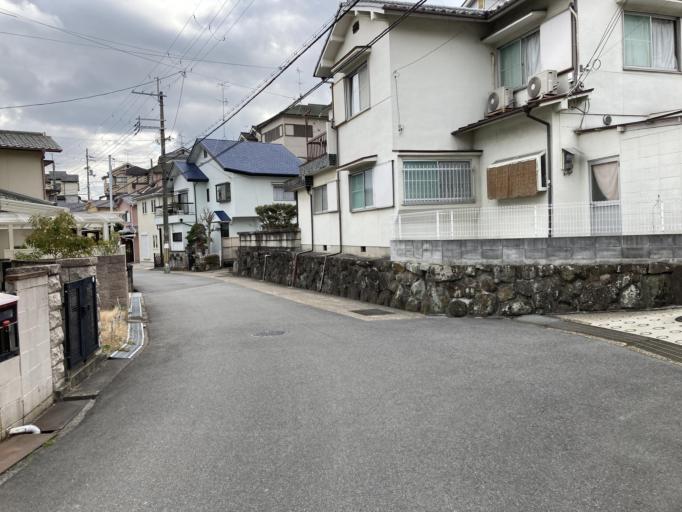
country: JP
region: Nara
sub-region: Ikoma-shi
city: Ikoma
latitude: 34.7104
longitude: 135.6975
